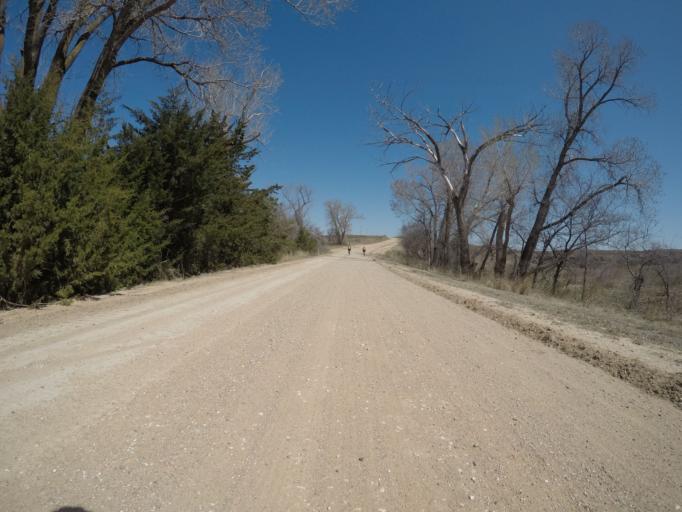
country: US
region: Kansas
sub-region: Pratt County
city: Pratt
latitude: 37.4039
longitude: -98.8407
